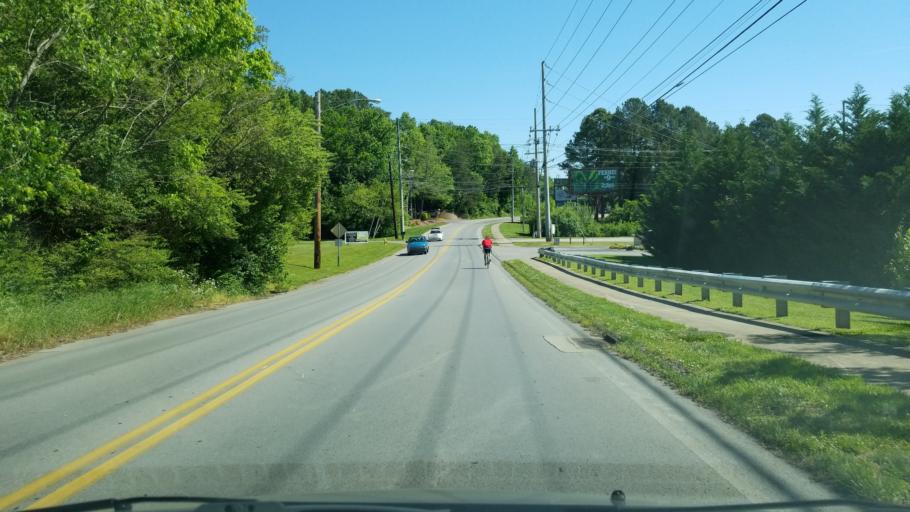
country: US
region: Tennessee
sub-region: Hamilton County
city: Red Bank
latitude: 35.1173
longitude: -85.3176
